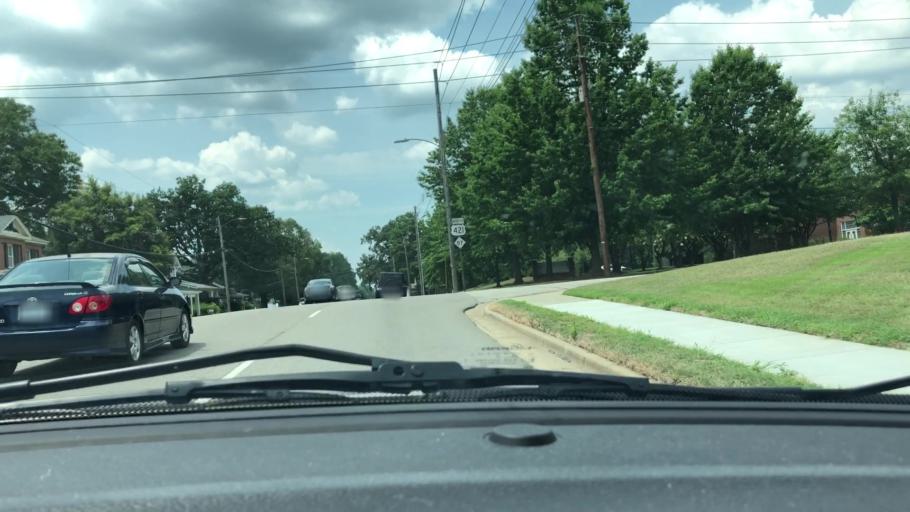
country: US
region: North Carolina
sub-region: Lee County
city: Sanford
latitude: 35.4814
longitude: -79.1818
